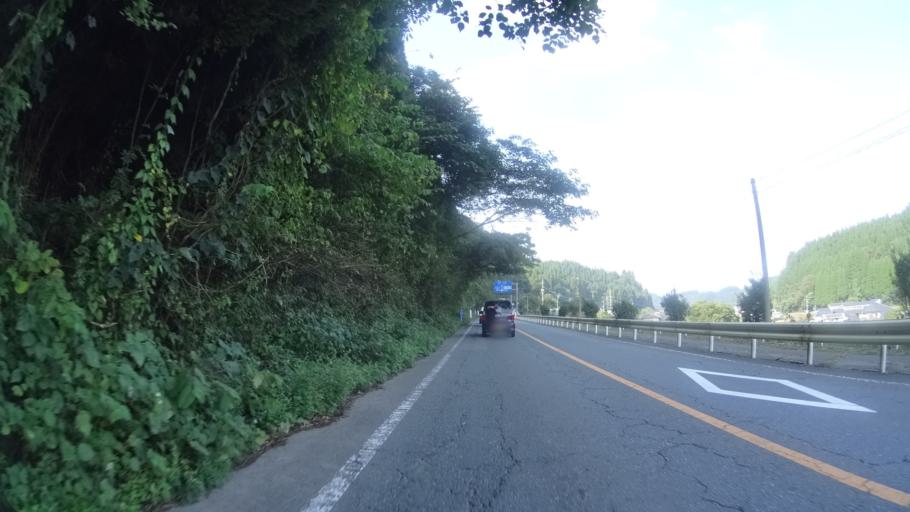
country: JP
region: Kumamoto
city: Aso
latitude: 33.0913
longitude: 131.0671
